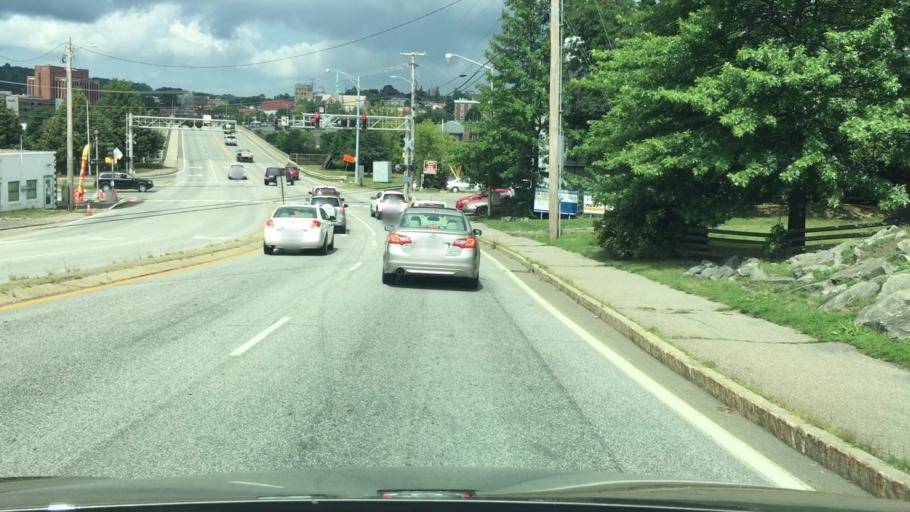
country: US
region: Maine
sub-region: Penobscot County
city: Brewer
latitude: 44.7975
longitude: -68.7616
